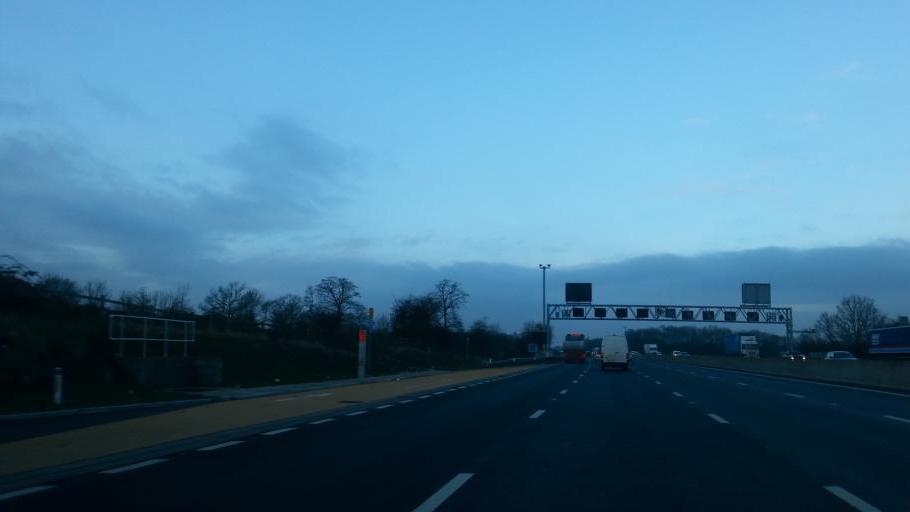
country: GB
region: England
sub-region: Worcestershire
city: Droitwich
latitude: 52.2485
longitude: -2.1335
